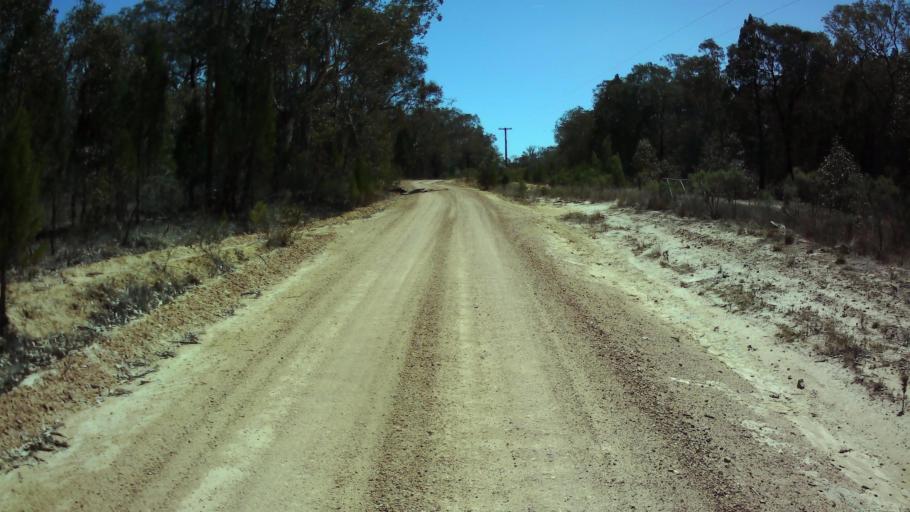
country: AU
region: New South Wales
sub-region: Cowra
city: Cowra
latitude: -33.8449
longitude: 148.4514
